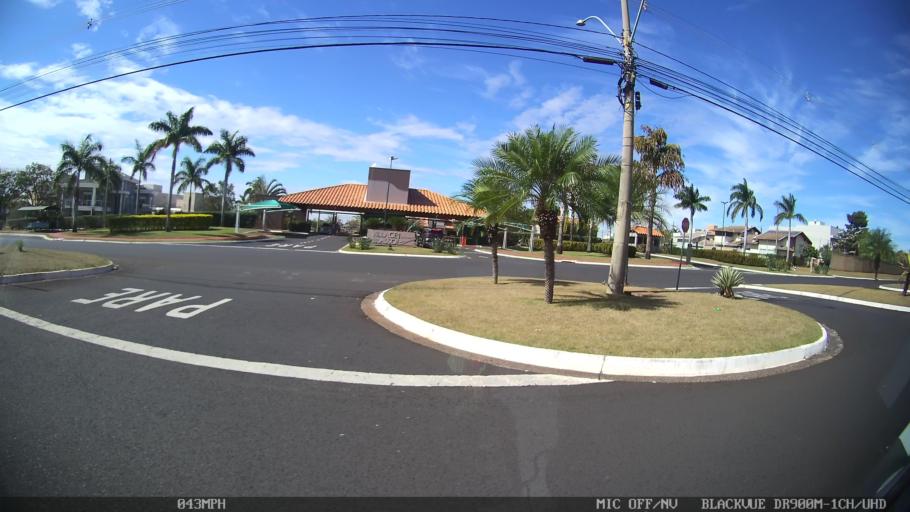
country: BR
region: Sao Paulo
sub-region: Sao Jose Do Rio Preto
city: Sao Jose do Rio Preto
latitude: -20.8219
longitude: -49.4817
